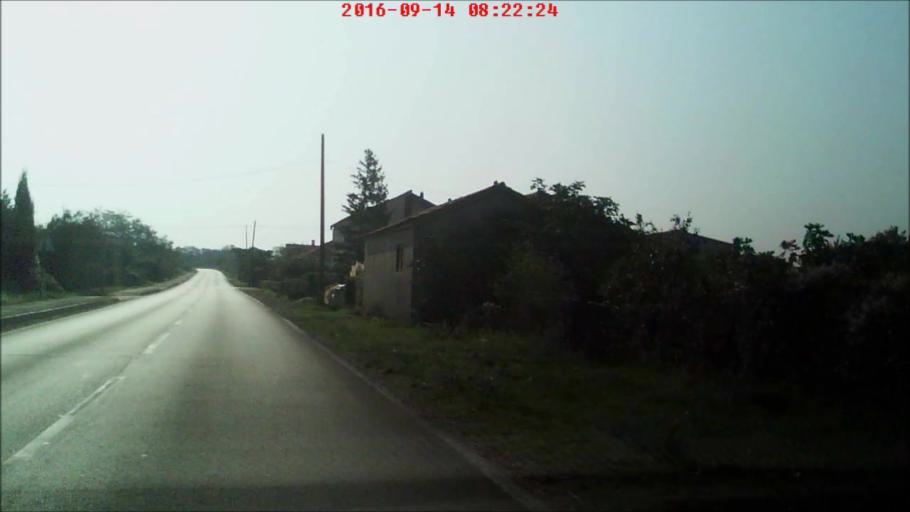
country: HR
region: Zadarska
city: Nin
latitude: 44.2179
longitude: 15.2186
